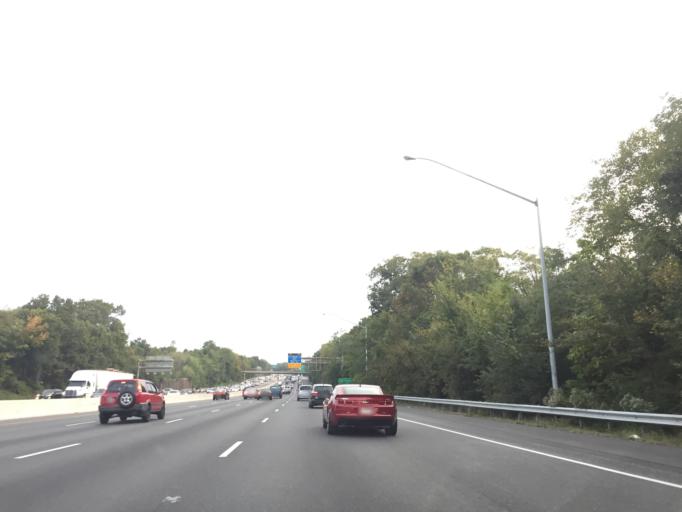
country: US
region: Maryland
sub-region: Prince George's County
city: Glenarden
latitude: 38.9349
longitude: -76.8553
